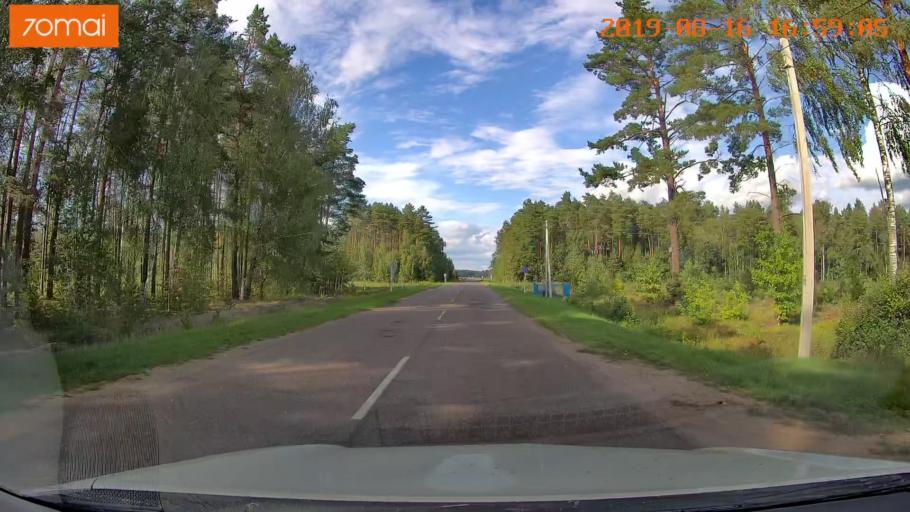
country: BY
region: Mogilev
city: Hlusha
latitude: 53.2779
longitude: 28.8390
